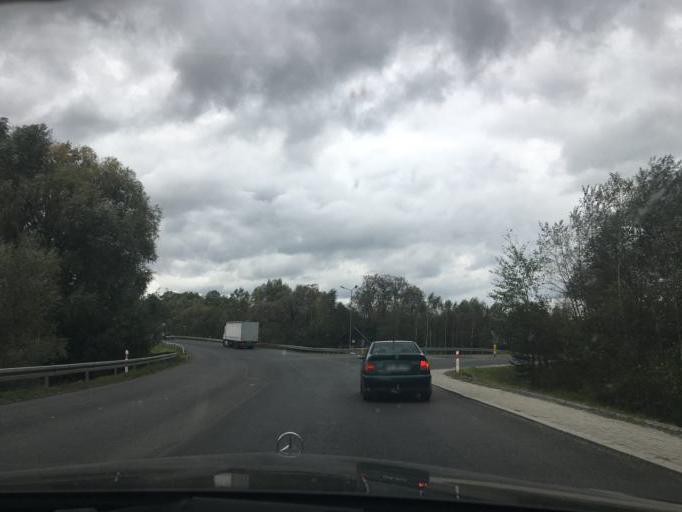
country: PL
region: Subcarpathian Voivodeship
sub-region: Powiat krosnienski
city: Kroscienko Wyzne
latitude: 49.6759
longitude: 21.8509
